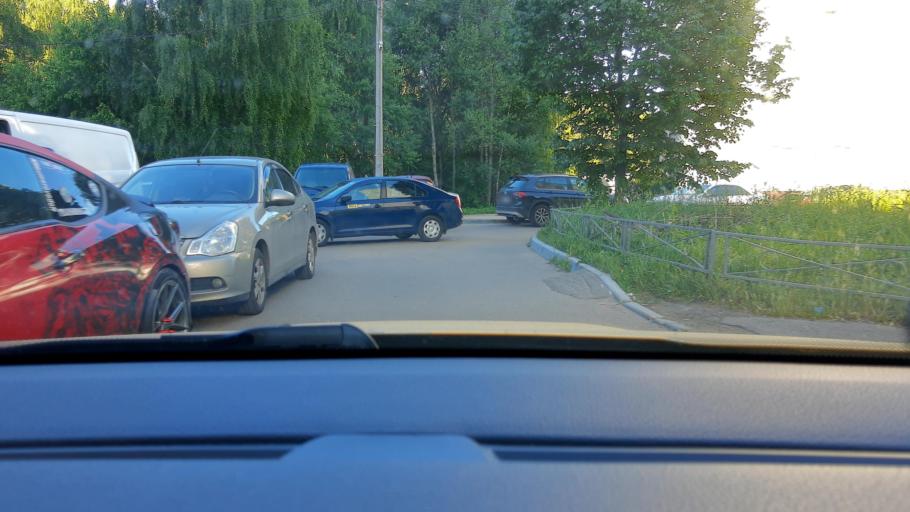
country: RU
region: Moscow
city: Khimki
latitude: 55.8783
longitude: 37.4210
